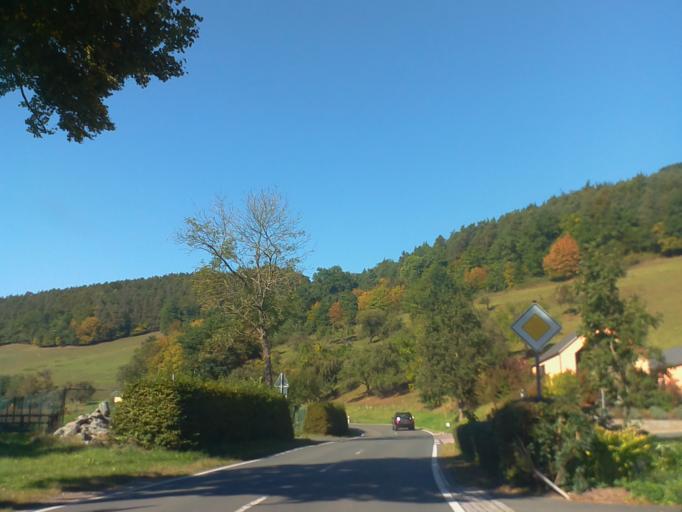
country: DE
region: Thuringia
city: Weissbach
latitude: 50.8290
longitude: 11.7929
